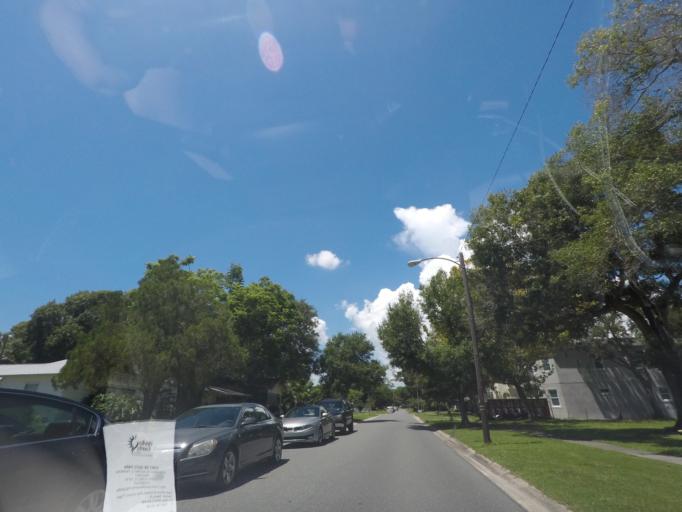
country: US
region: Florida
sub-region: Pinellas County
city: Lealman
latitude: 27.8037
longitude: -82.6396
